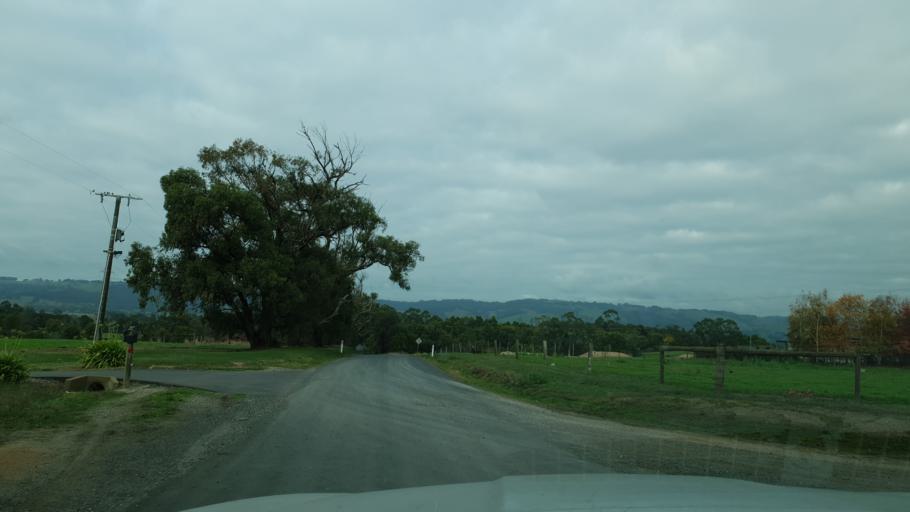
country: AU
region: Victoria
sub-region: Latrobe
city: Moe
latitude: -38.1735
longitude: 146.1309
